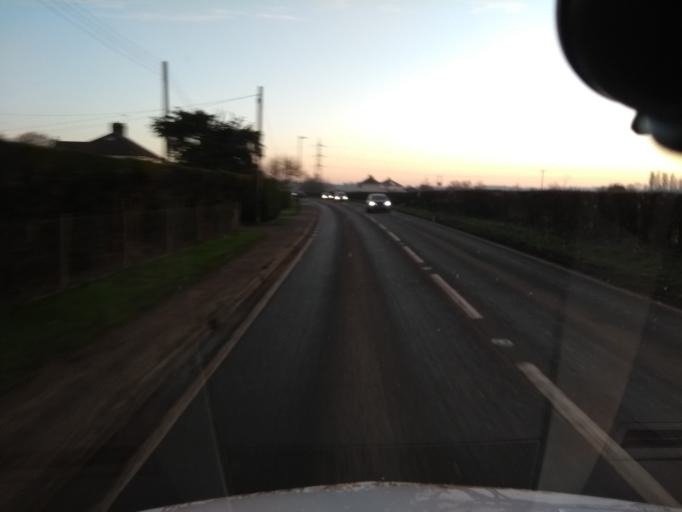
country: GB
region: England
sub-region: Somerset
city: Puriton
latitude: 51.1471
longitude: -2.9677
